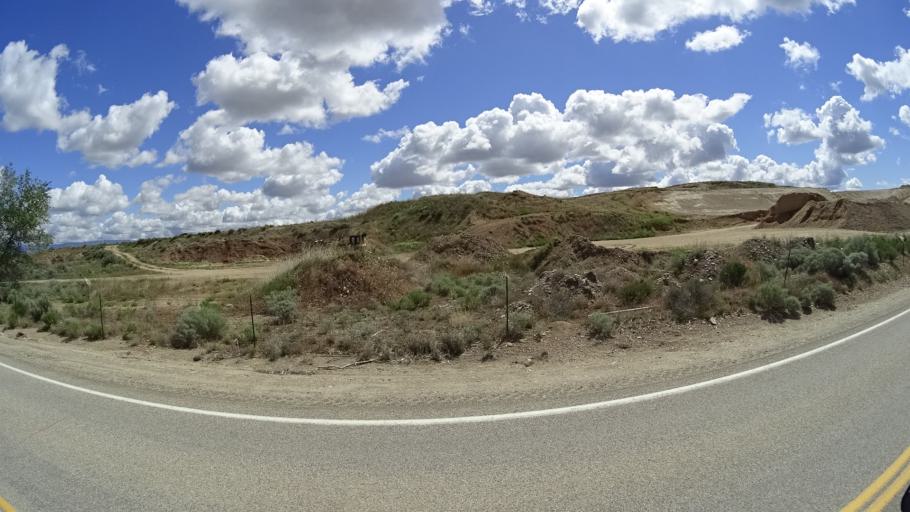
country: US
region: Idaho
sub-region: Ada County
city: Kuna
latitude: 43.5149
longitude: -116.3149
